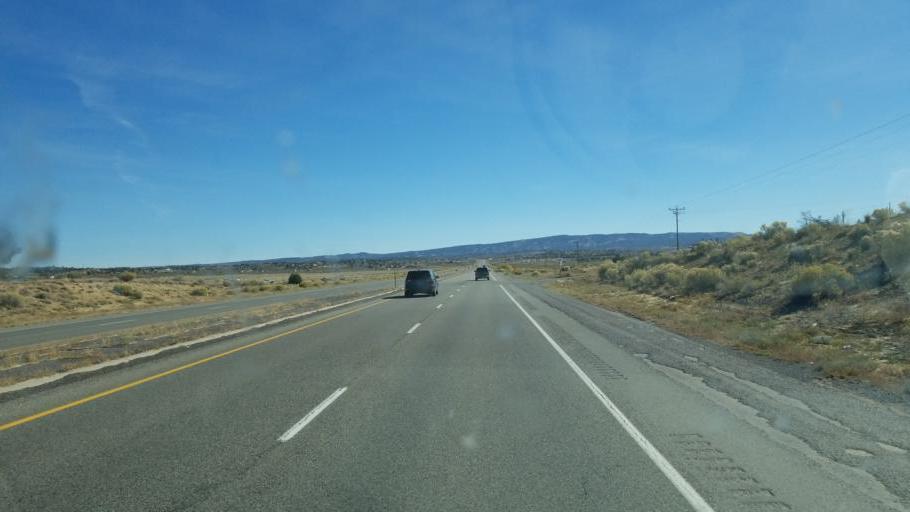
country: US
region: New Mexico
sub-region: McKinley County
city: Twin Lakes
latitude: 35.6352
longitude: -108.8296
